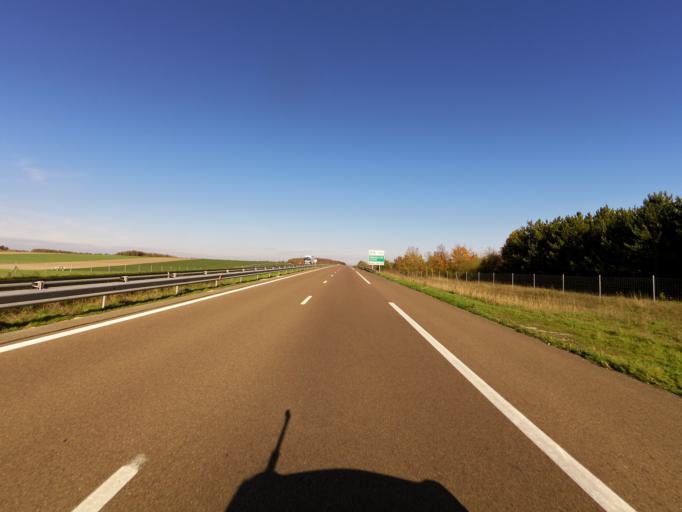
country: FR
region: Champagne-Ardenne
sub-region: Departement de la Marne
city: Compertrix
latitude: 48.8933
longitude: 4.2877
